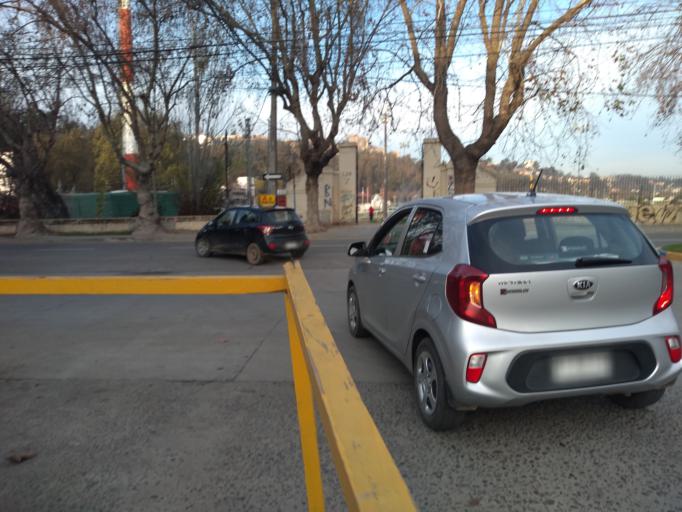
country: CL
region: Valparaiso
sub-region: Provincia de Valparaiso
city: Vina del Mar
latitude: -33.0204
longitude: -71.5413
